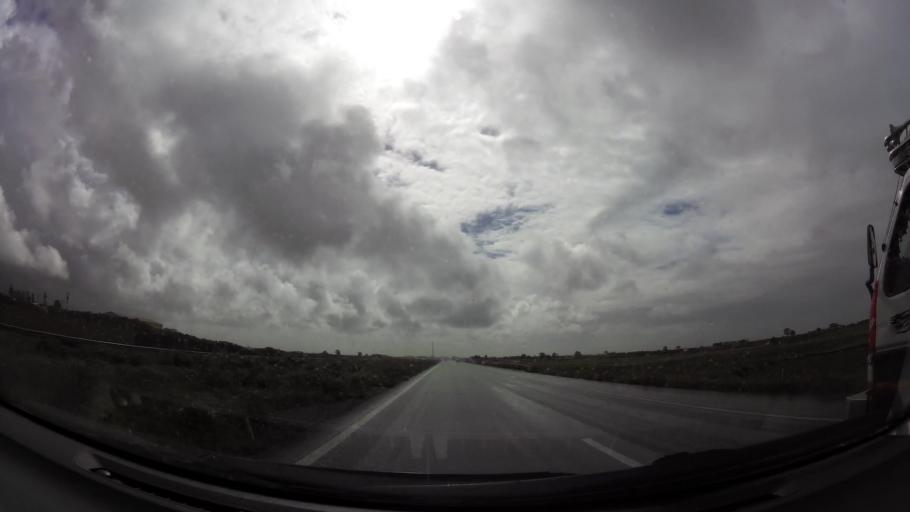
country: MA
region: Grand Casablanca
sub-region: Nouaceur
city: Dar Bouazza
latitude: 33.3909
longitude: -7.8709
